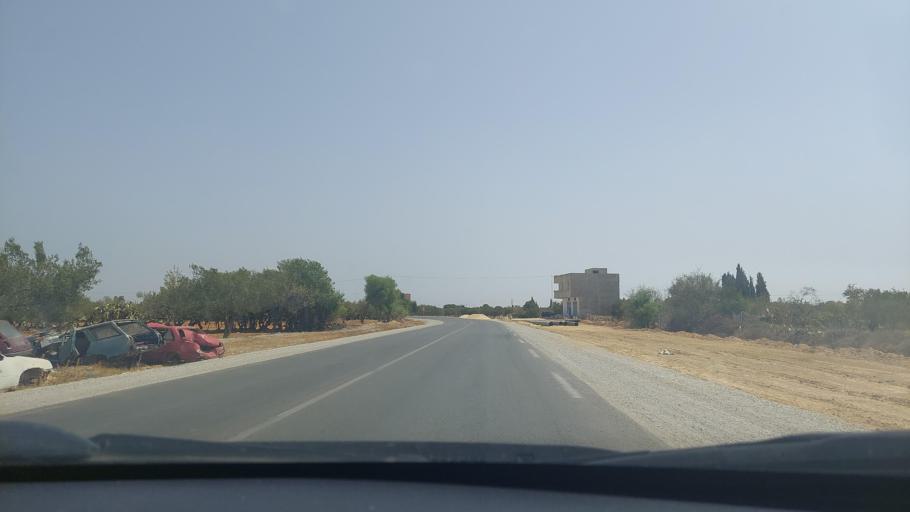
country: TN
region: Al Munastir
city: Qasr Hallal
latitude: 35.6028
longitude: 10.8945
